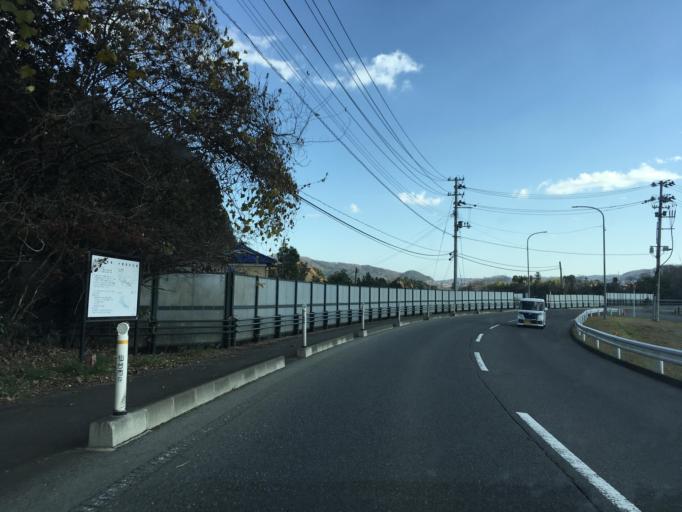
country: JP
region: Miyagi
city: Sendai
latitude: 38.2798
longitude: 140.7625
